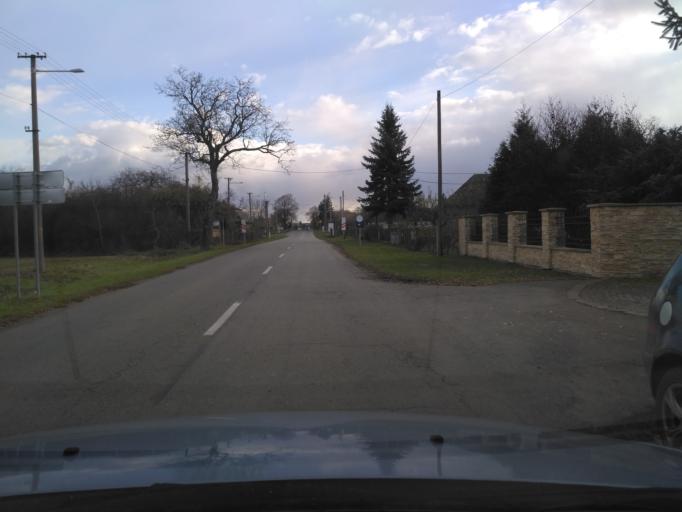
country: HU
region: Borsod-Abauj-Zemplen
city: Satoraljaujhely
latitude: 48.3922
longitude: 21.7517
